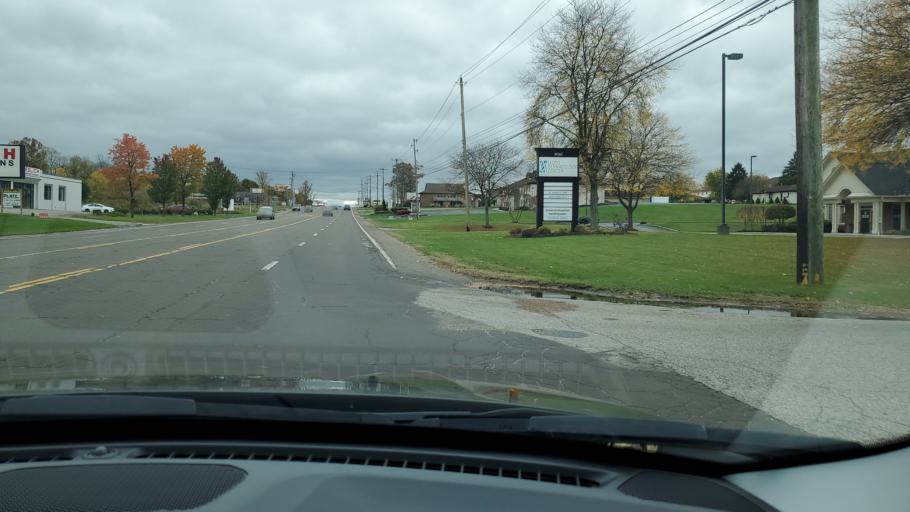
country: US
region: Ohio
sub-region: Mahoning County
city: Boardman
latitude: 41.0039
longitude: -80.6628
